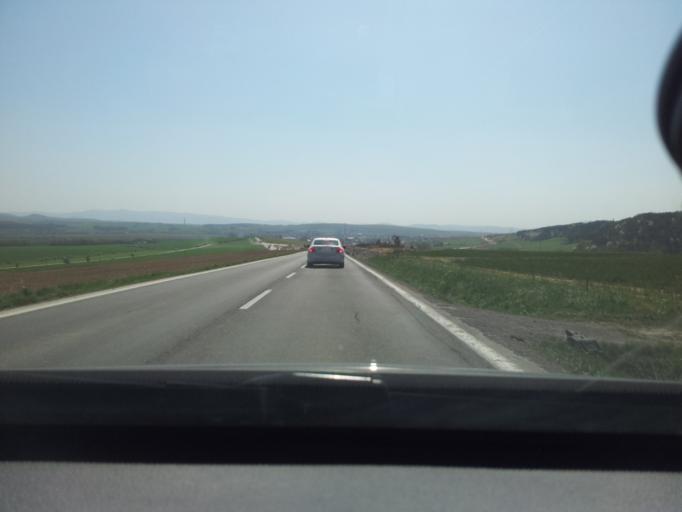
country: SK
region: Nitriansky
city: Banovce nad Bebravou
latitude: 48.7513
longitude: 18.2114
